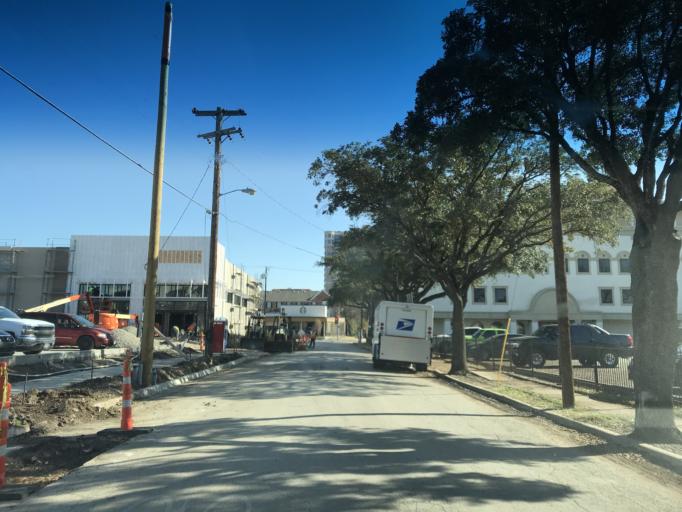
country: US
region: Texas
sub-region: Dallas County
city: Dallas
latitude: 32.8077
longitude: -96.8117
